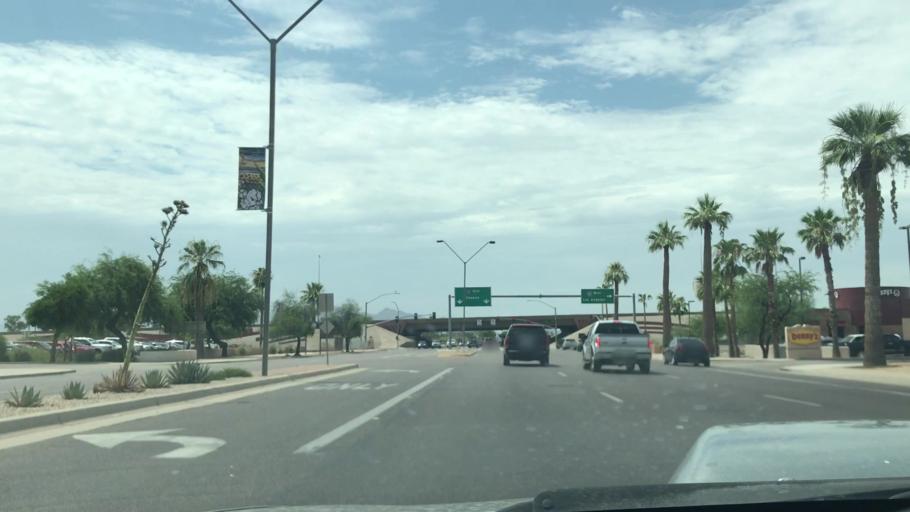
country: US
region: Arizona
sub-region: Maricopa County
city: Goodyear
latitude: 33.4603
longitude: -112.3582
